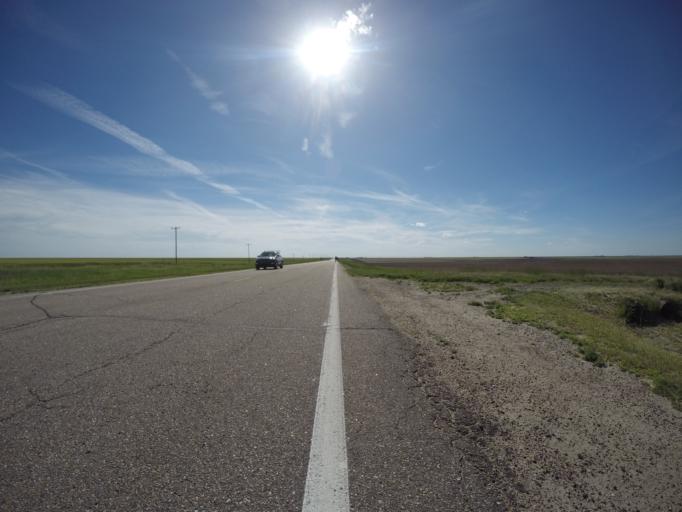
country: US
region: Kansas
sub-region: Cheyenne County
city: Saint Francis
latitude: 39.7566
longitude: -101.9937
